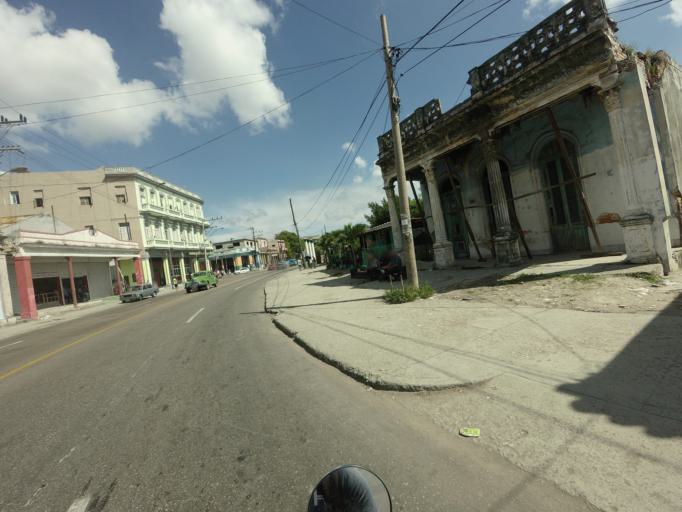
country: TM
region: Balkan
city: Gumdag
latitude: 38.8436
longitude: 54.1746
